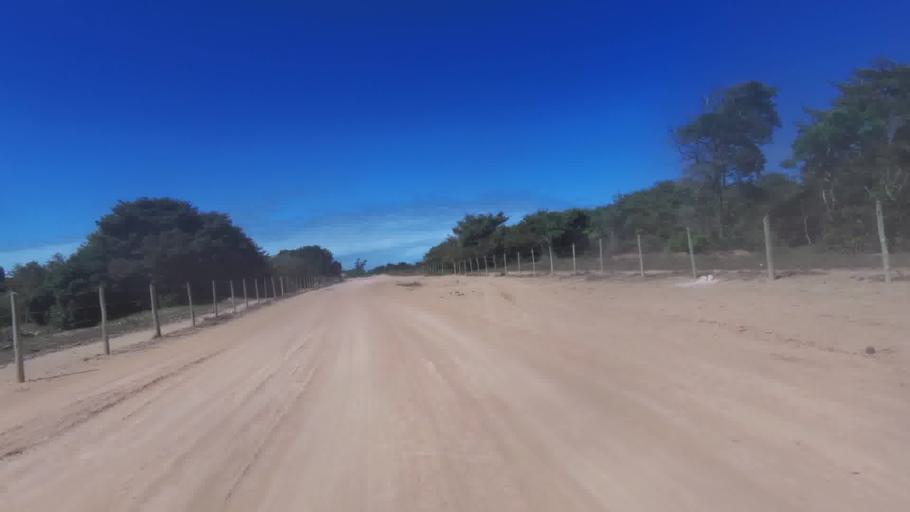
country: BR
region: Espirito Santo
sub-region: Marataizes
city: Marataizes
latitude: -21.1978
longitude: -40.9409
